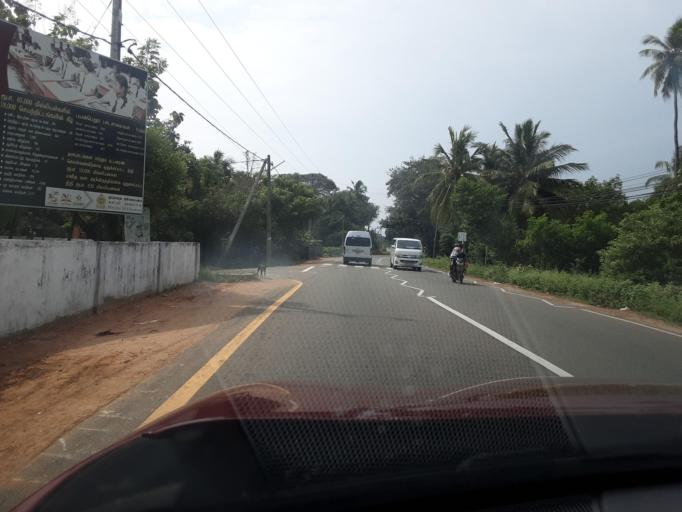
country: LK
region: Northern Province
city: Jaffna
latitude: 9.6605
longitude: 80.0481
